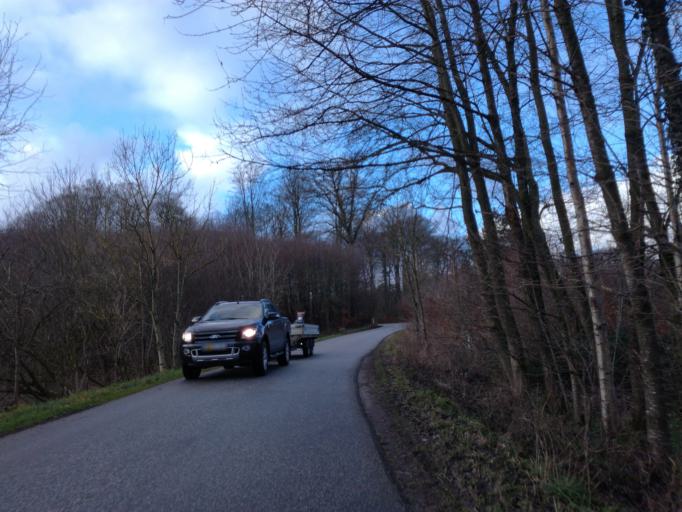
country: DK
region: South Denmark
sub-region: Fredericia Kommune
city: Taulov
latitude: 55.5654
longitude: 9.6297
